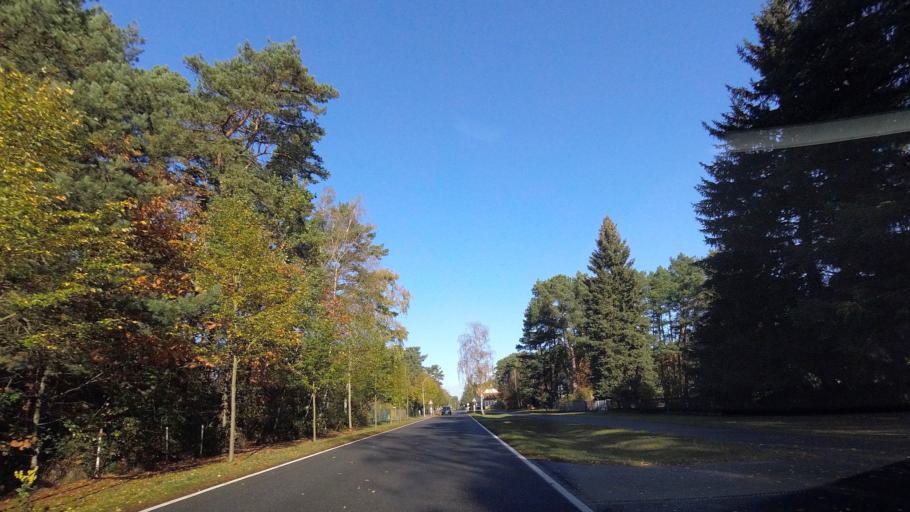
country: DE
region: Brandenburg
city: Borkheide
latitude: 52.2282
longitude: 12.8564
